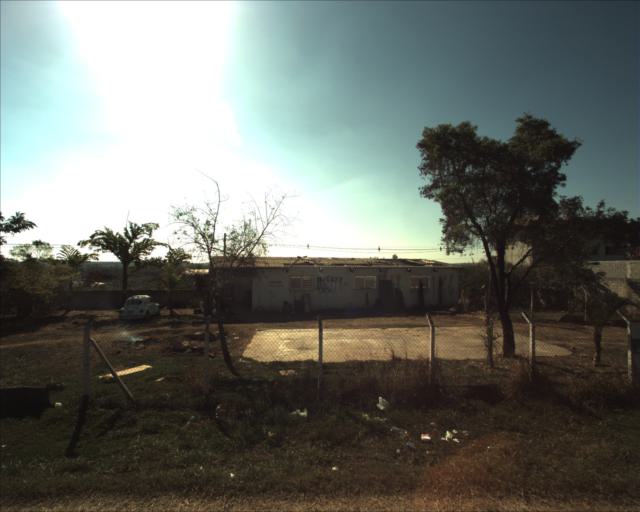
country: BR
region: Sao Paulo
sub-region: Sorocaba
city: Sorocaba
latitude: -23.4144
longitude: -47.3962
